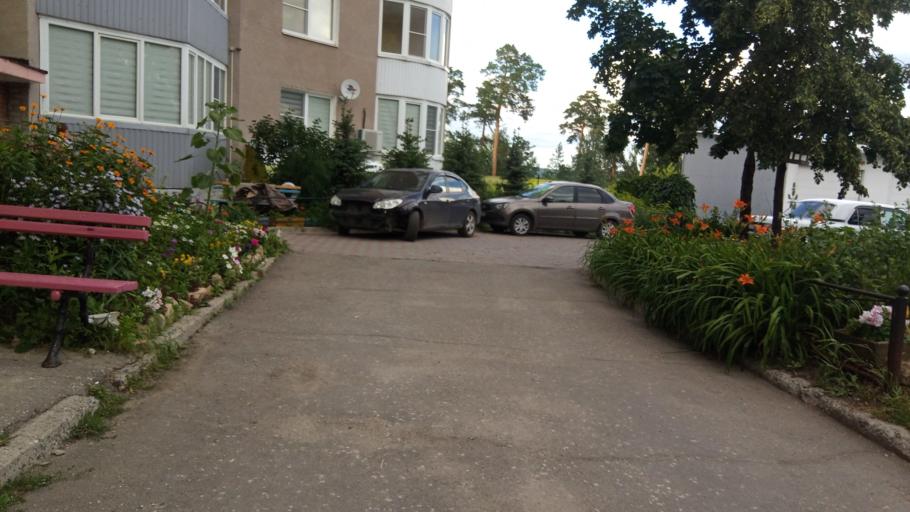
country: RU
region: Chelyabinsk
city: Chebarkul'
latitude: 55.0210
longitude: 60.3120
